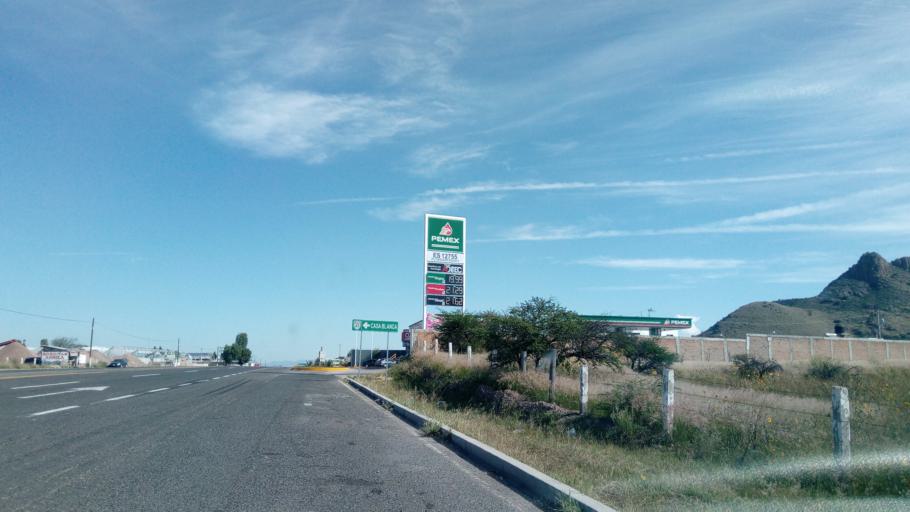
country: MX
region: Durango
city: Victoria de Durango
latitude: 24.1446
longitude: -104.7098
